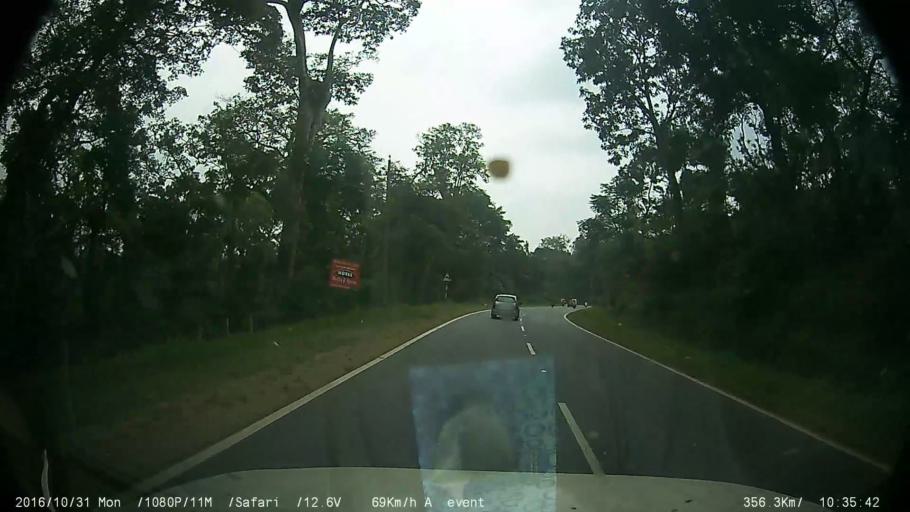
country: IN
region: Karnataka
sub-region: Kodagu
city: Suntikoppa
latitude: 12.4454
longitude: 75.8473
